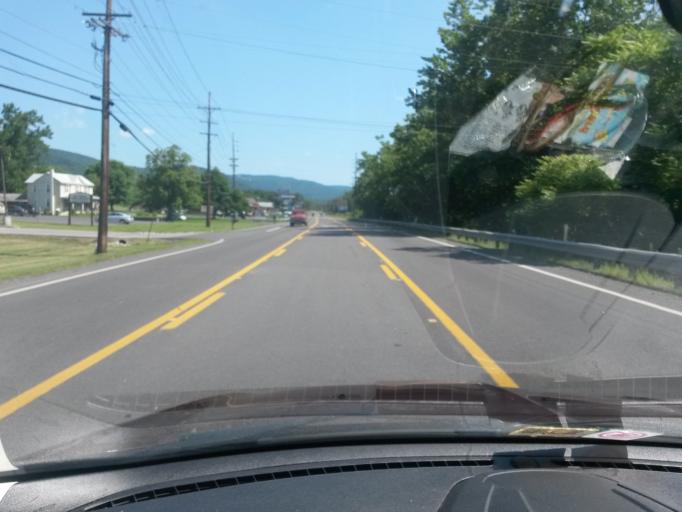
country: US
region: West Virginia
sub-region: Mineral County
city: Keyser
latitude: 39.4113
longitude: -79.0009
